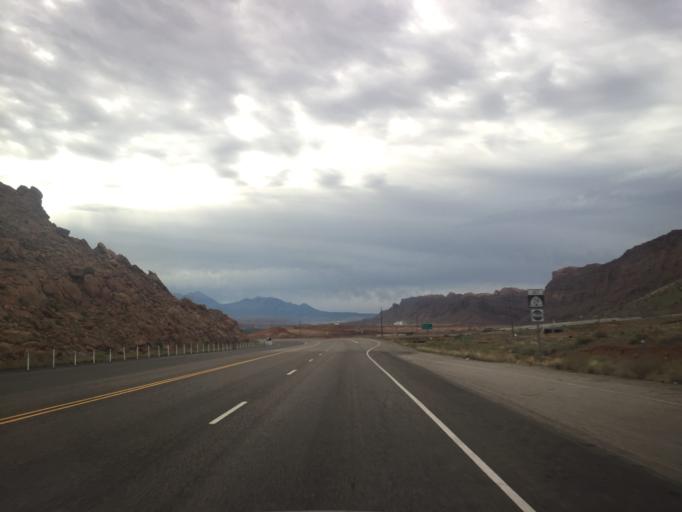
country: US
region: Utah
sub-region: Grand County
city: Moab
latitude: 38.6076
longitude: -109.6042
